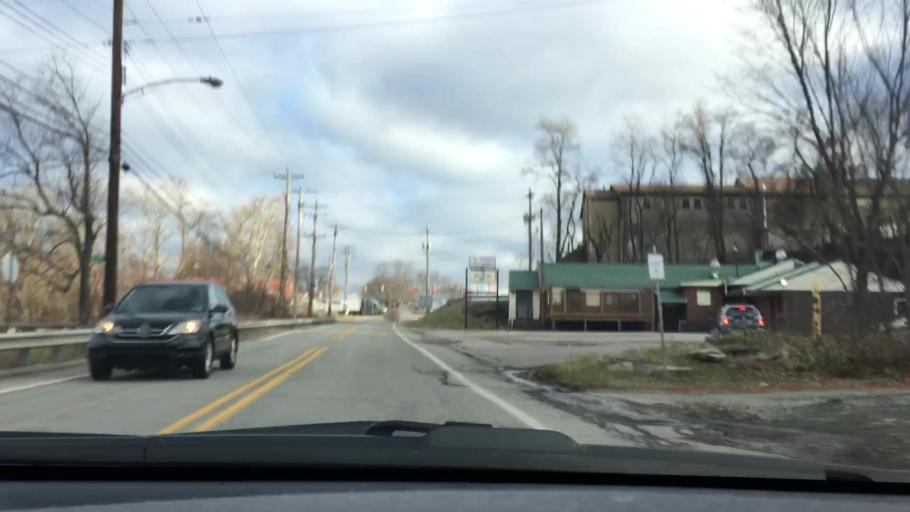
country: US
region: Pennsylvania
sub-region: Allegheny County
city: East McKeesport
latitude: 40.3739
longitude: -79.7980
